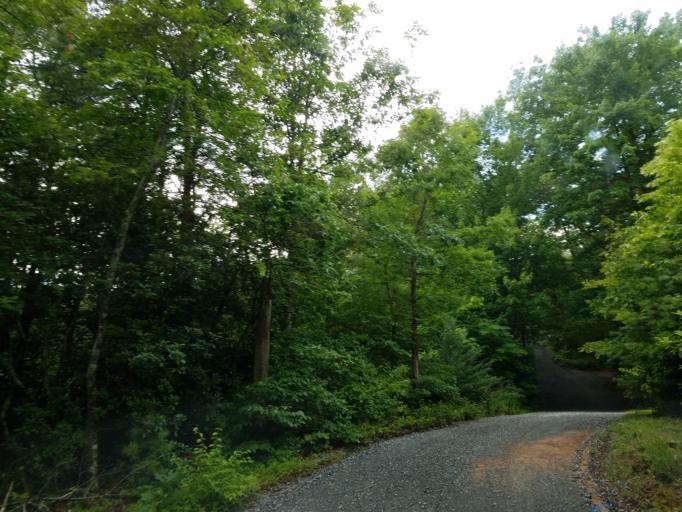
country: US
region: Georgia
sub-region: Fannin County
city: Blue Ridge
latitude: 34.7965
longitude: -84.2892
